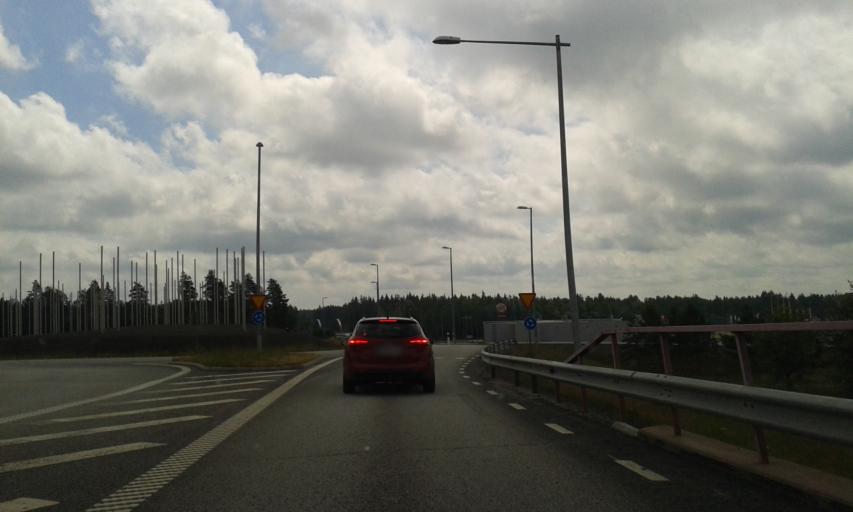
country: SE
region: Joenkoeping
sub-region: Gislaveds Kommun
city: Gislaved
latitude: 57.3245
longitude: 13.5438
